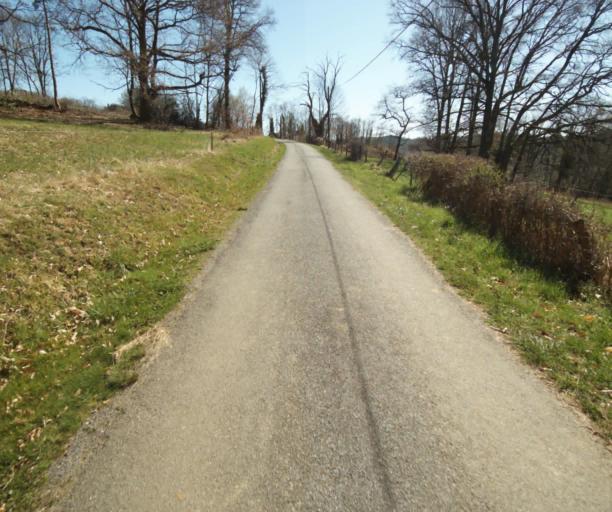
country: FR
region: Limousin
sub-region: Departement de la Correze
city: Uzerche
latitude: 45.4061
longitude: 1.6191
